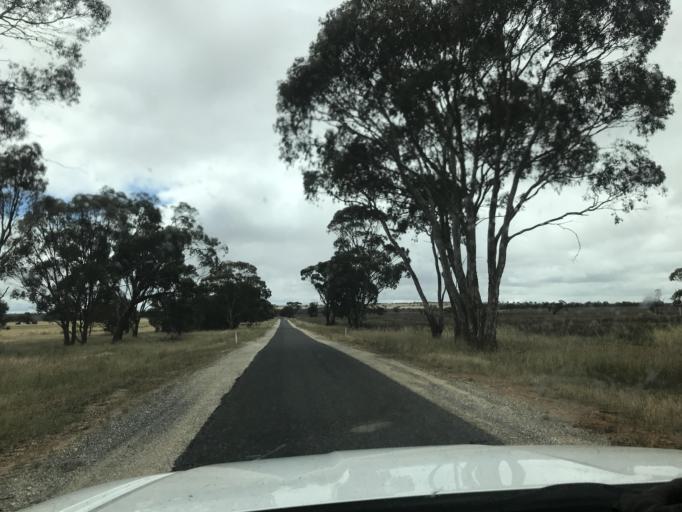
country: AU
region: South Australia
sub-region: Tatiara
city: Bordertown
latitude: -36.3260
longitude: 141.3565
